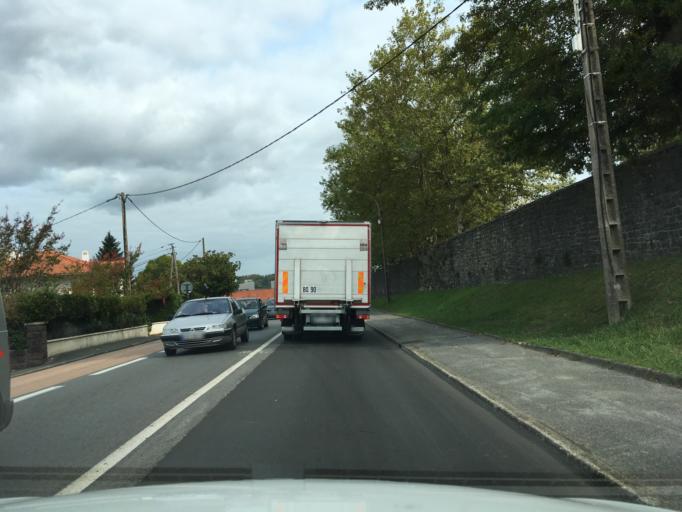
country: FR
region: Aquitaine
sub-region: Departement des Pyrenees-Atlantiques
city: Bayonne
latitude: 43.4850
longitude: -1.4661
